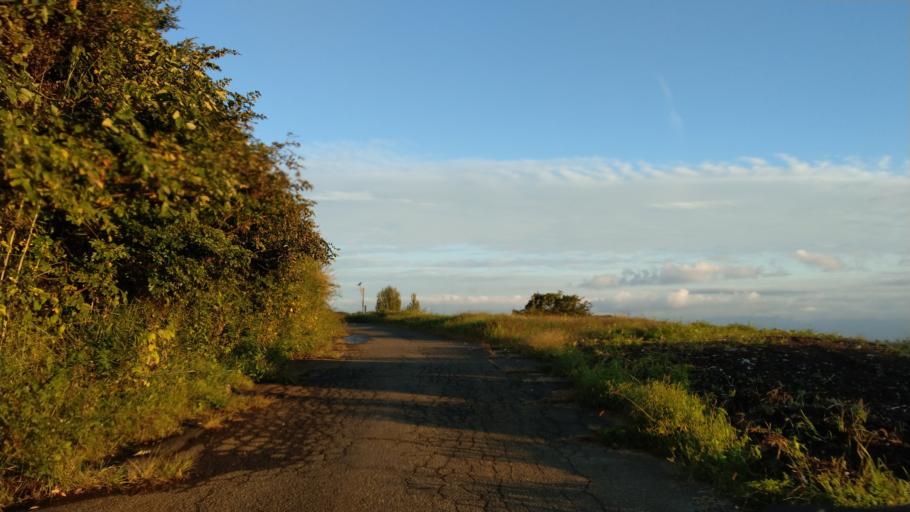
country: JP
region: Nagano
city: Komoro
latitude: 36.3465
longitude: 138.4248
